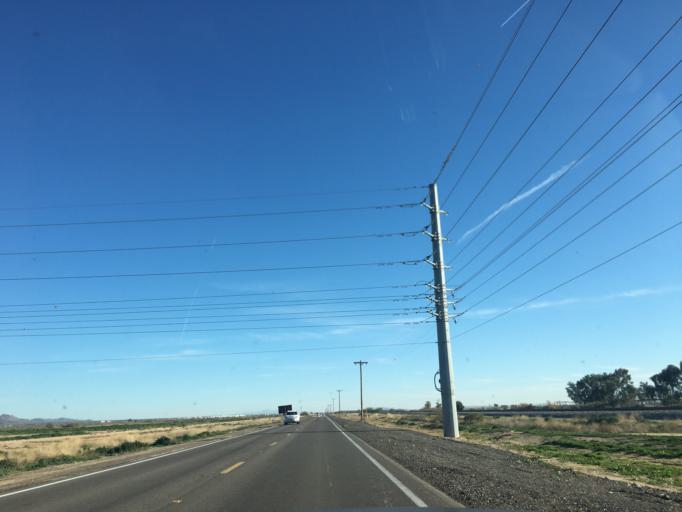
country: US
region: Arizona
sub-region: Pinal County
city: Maricopa
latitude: 33.0136
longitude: -111.9782
